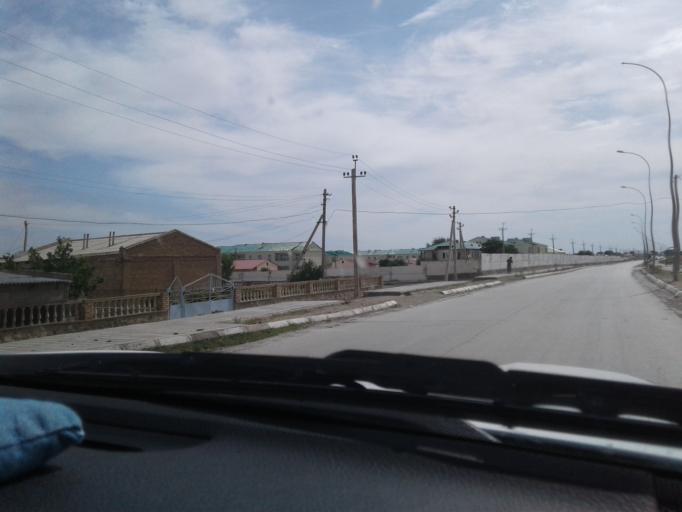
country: TM
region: Balkan
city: Gazanjyk
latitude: 39.2450
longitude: 55.4901
